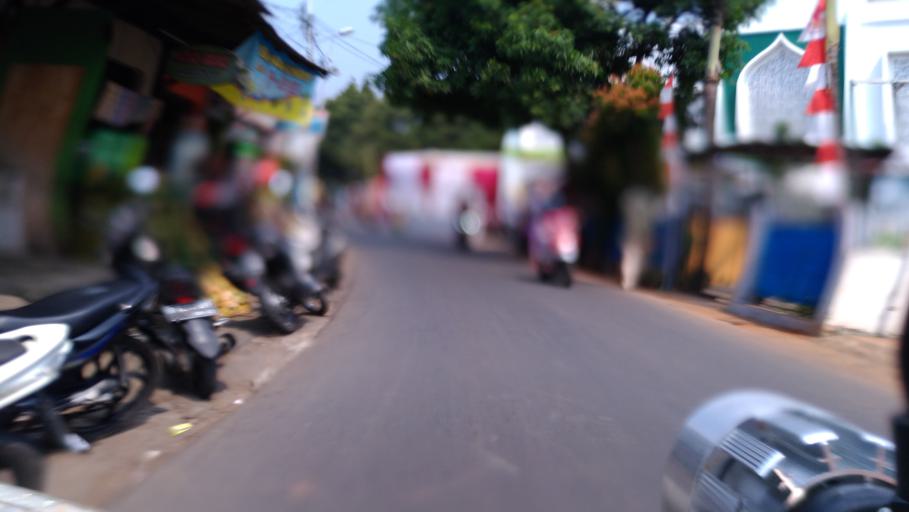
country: ID
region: West Java
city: Depok
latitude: -6.3537
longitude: 106.8783
